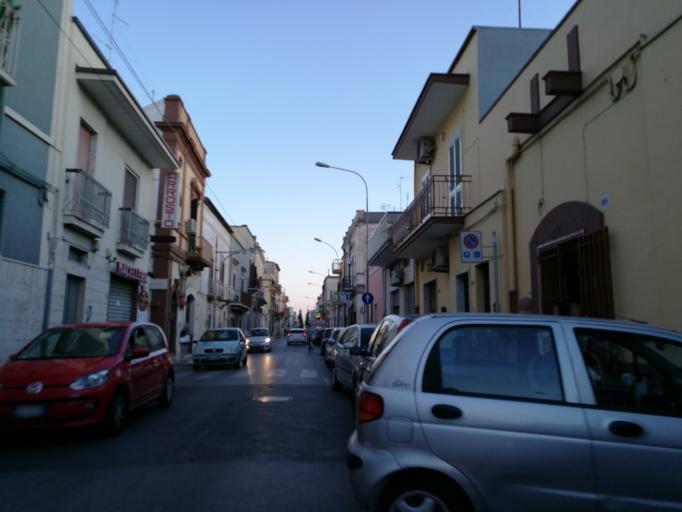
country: IT
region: Apulia
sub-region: Provincia di Bari
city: Valenzano
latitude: 41.0640
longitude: 16.8688
